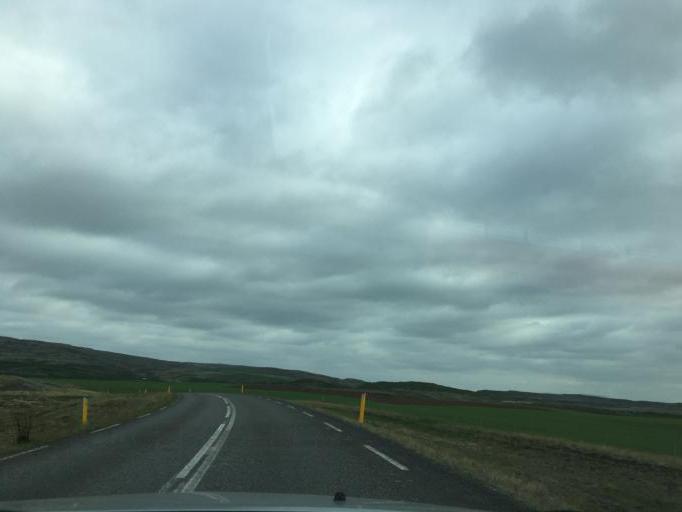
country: IS
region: South
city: Vestmannaeyjar
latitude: 64.2708
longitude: -20.2265
